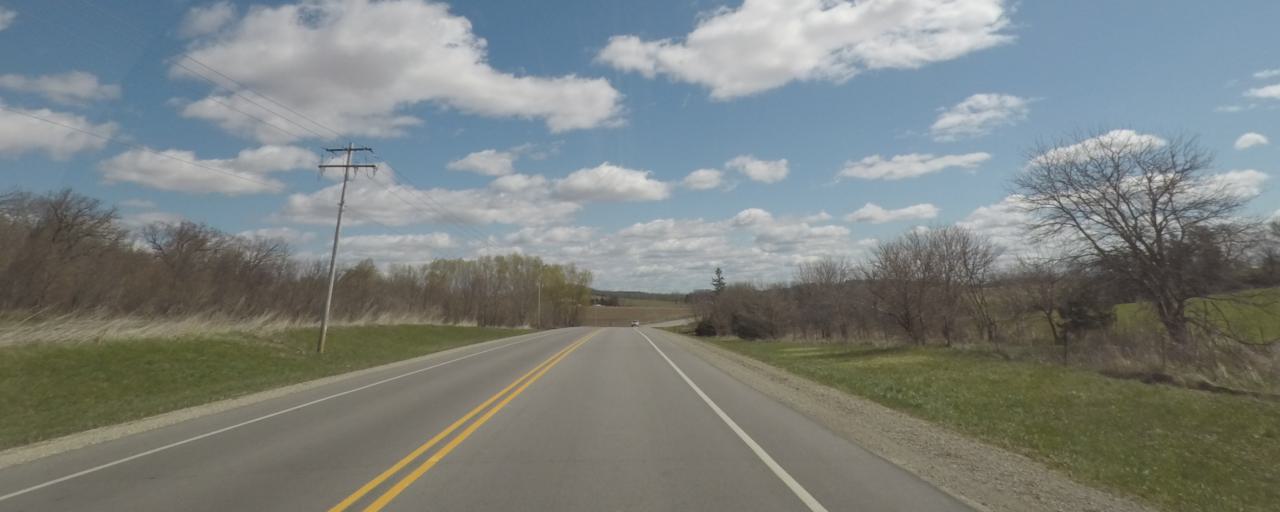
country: US
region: Wisconsin
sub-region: Jefferson County
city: Lake Mills
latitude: 43.0848
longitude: -88.9897
